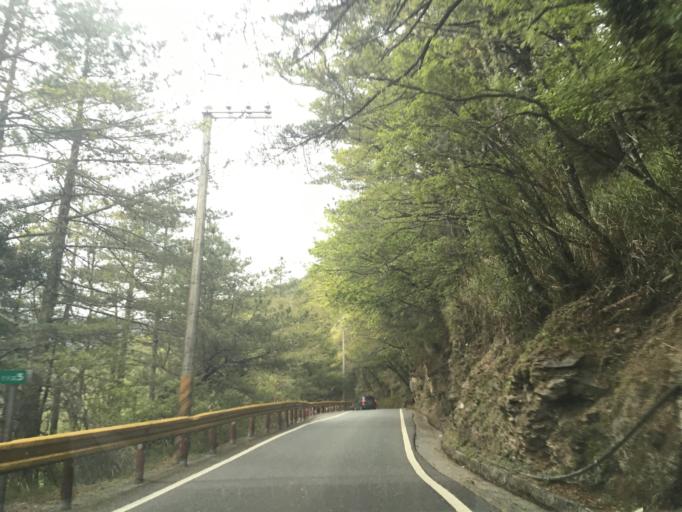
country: TW
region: Taiwan
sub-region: Hualien
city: Hualian
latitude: 24.1805
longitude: 121.3225
